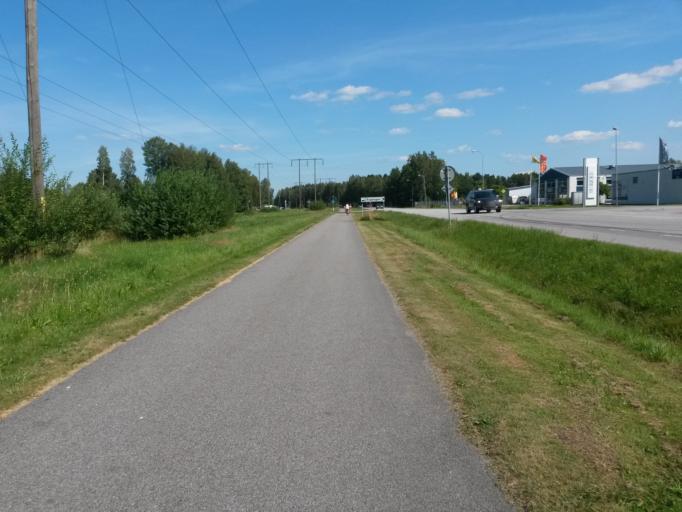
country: SE
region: Vaestra Goetaland
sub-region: Lidkopings Kommun
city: Lidkoping
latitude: 58.4963
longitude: 13.1845
